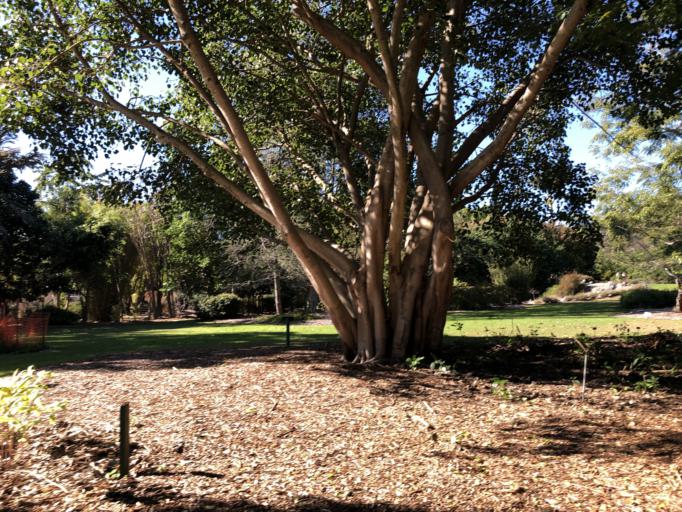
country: AU
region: New South Wales
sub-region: Coffs Harbour
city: Coffs Harbour
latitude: -30.2927
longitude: 153.1246
